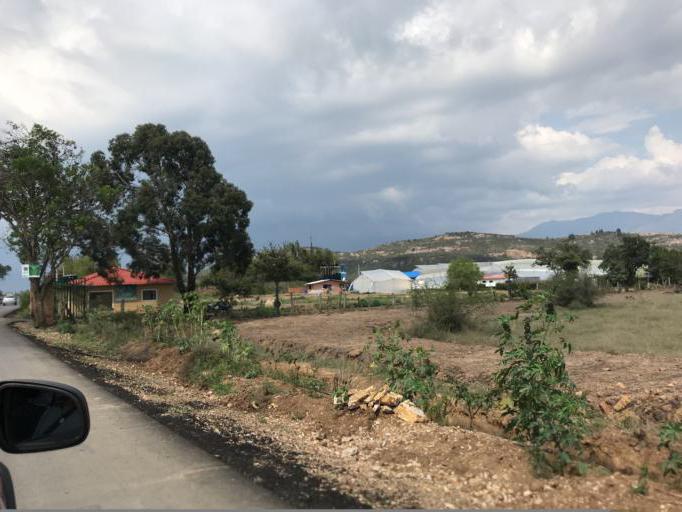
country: CO
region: Boyaca
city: Sutamarchan
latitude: 5.6361
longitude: -73.5997
